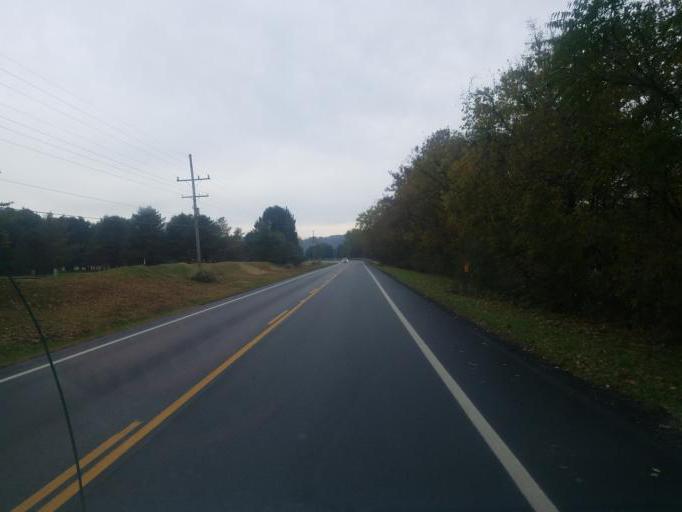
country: US
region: Ohio
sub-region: Washington County
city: Beverly
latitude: 39.5521
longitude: -81.6089
